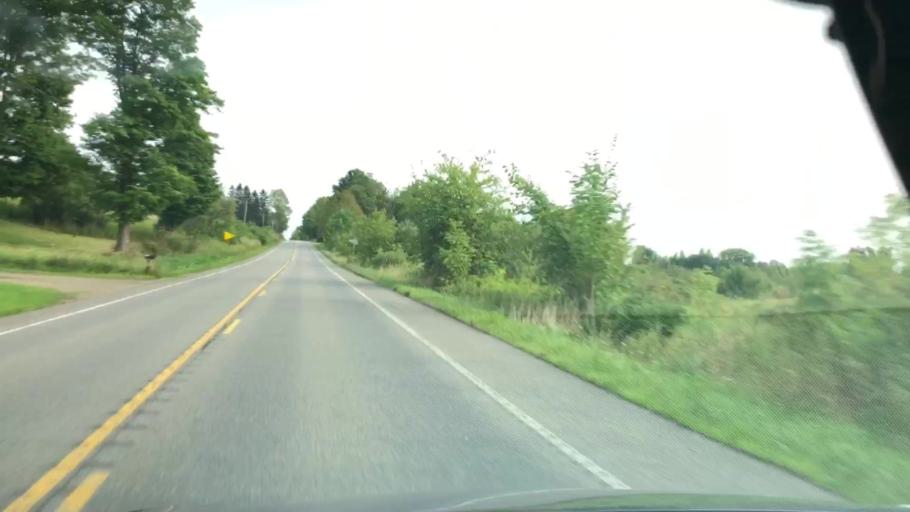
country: US
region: Pennsylvania
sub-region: Erie County
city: Union City
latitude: 41.8489
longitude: -79.8238
